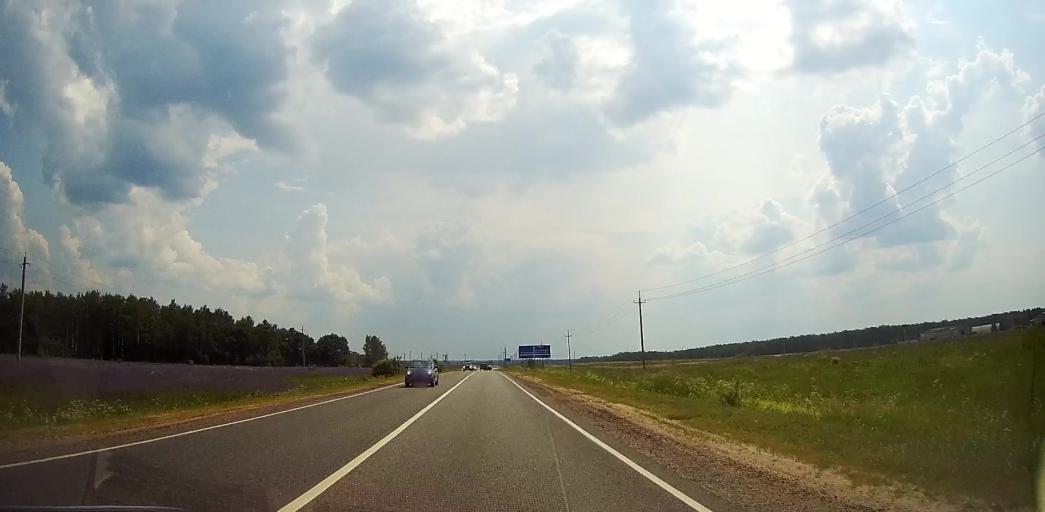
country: RU
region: Moskovskaya
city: Stupino
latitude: 54.9599
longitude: 38.1233
